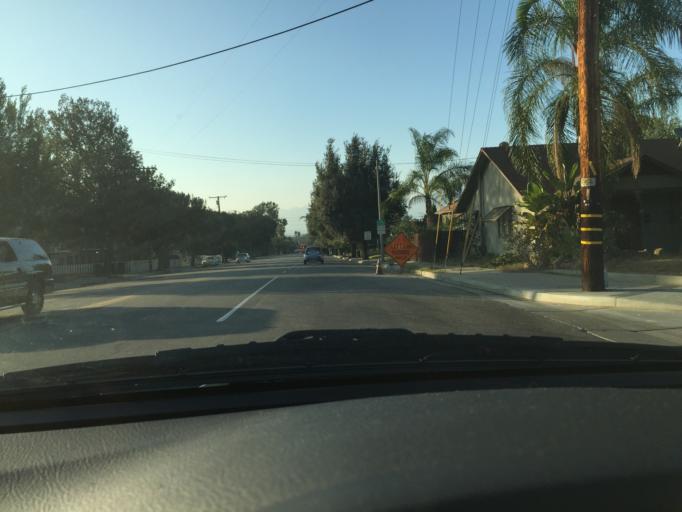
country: US
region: California
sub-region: San Bernardino County
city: Redlands
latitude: 34.0454
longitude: -117.1958
